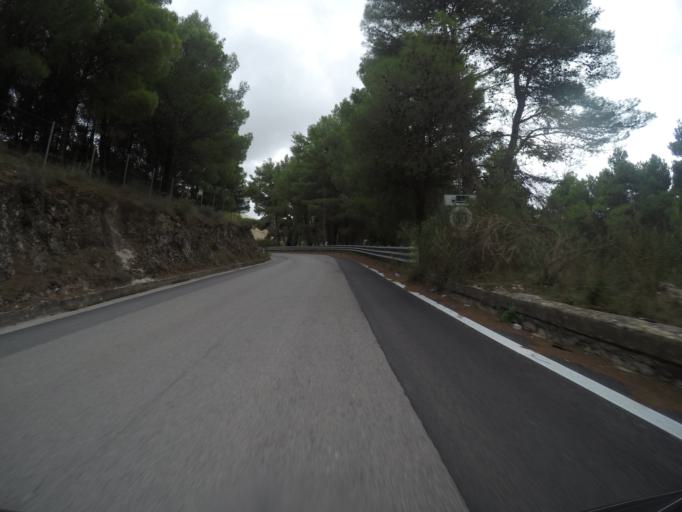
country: IT
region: Sicily
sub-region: Palermo
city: Montelepre
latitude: 38.1067
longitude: 13.1695
